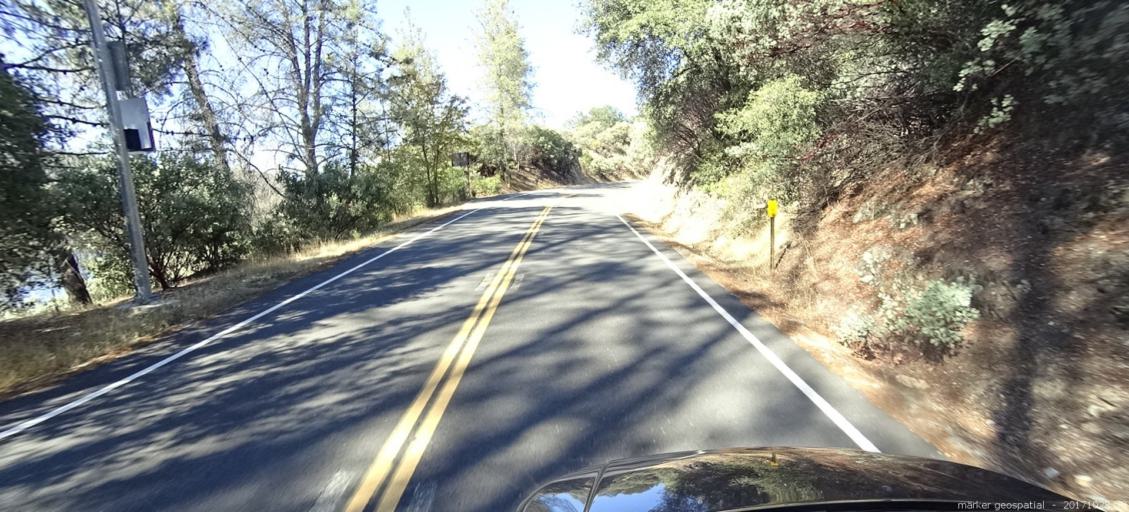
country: US
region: California
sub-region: Shasta County
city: Shasta
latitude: 40.6019
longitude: -122.5358
